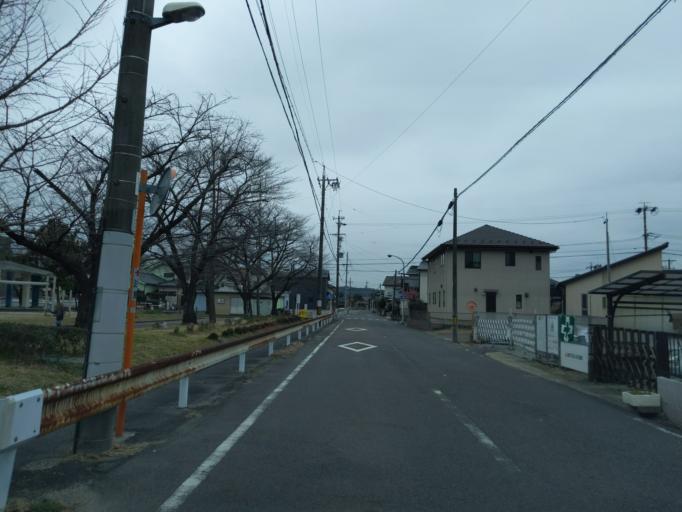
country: JP
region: Aichi
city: Kasugai
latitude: 35.2513
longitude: 136.9891
